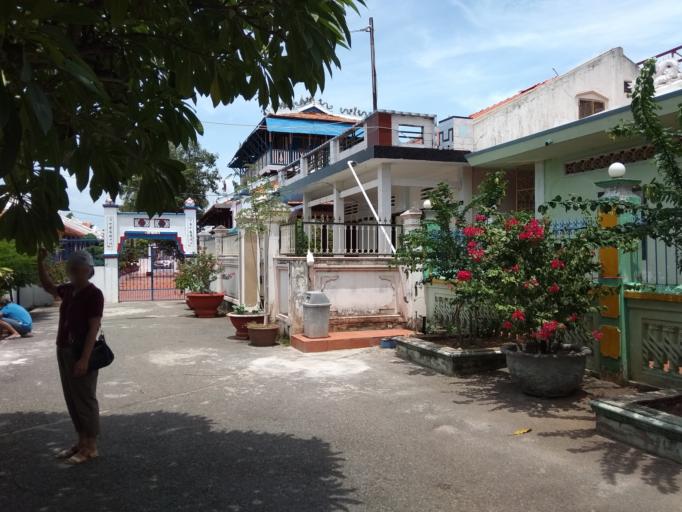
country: VN
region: Ba Ria-Vung Tau
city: Thanh Pho Ba Ria
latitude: 10.4546
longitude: 107.0965
